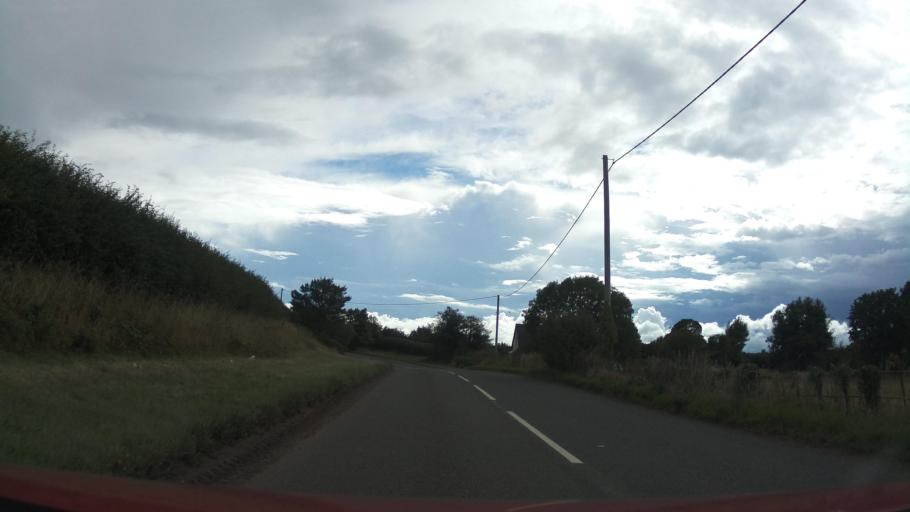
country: GB
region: England
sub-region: Shropshire
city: Woodcote
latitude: 52.7266
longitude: -2.3487
